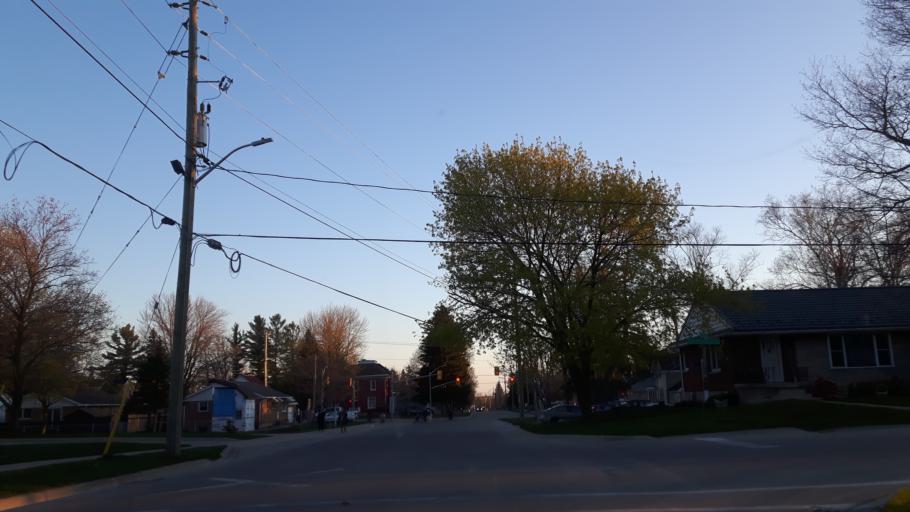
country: CA
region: Ontario
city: Bluewater
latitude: 43.6150
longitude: -81.5320
